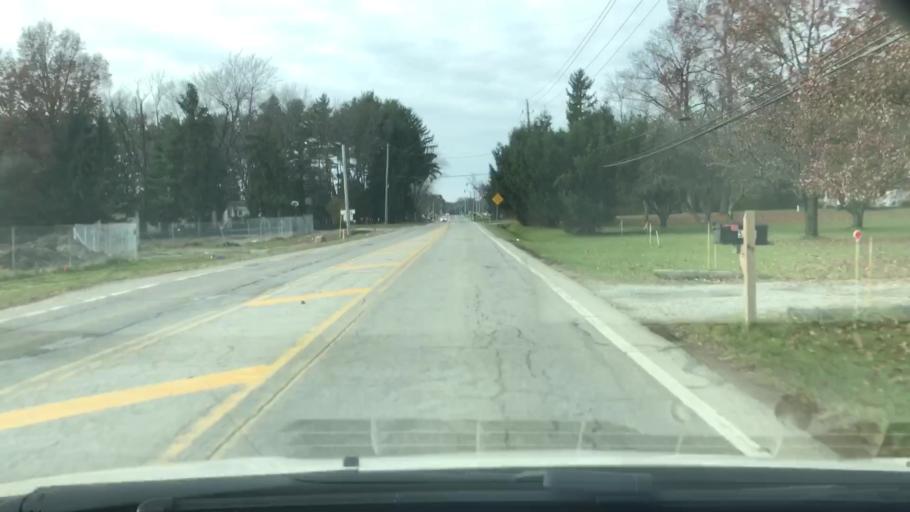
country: US
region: Ohio
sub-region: Franklin County
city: New Albany
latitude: 40.1000
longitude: -82.8500
